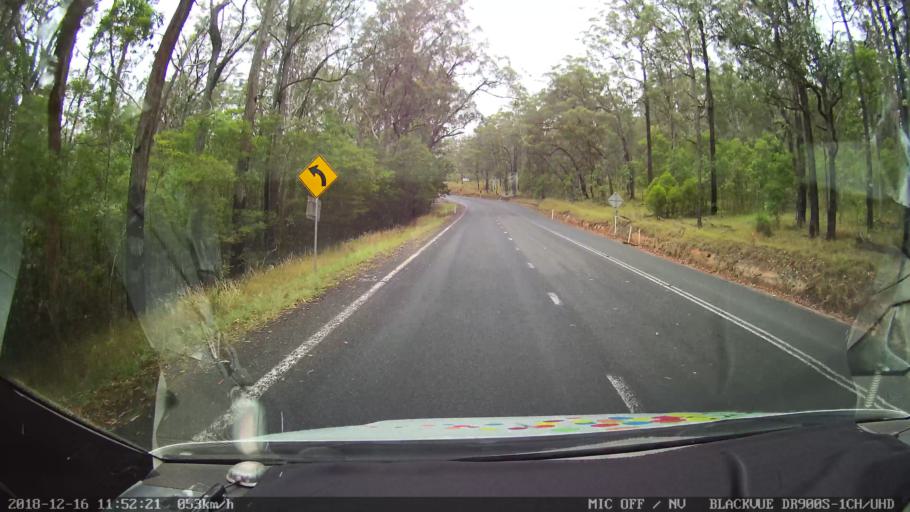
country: AU
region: New South Wales
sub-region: Tenterfield Municipality
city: Carrolls Creek
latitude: -28.9034
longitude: 152.2716
